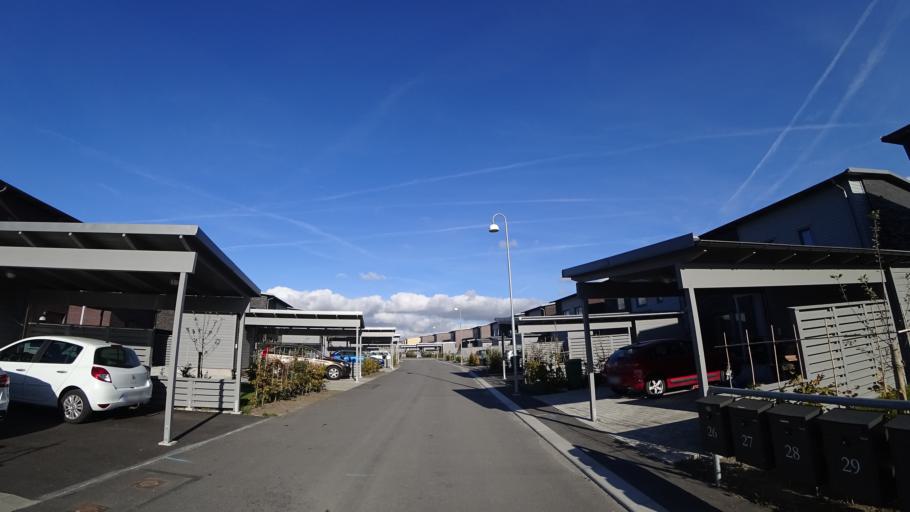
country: SE
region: Skane
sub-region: Staffanstorps Kommun
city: Hjaerup
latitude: 55.6712
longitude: 13.1532
